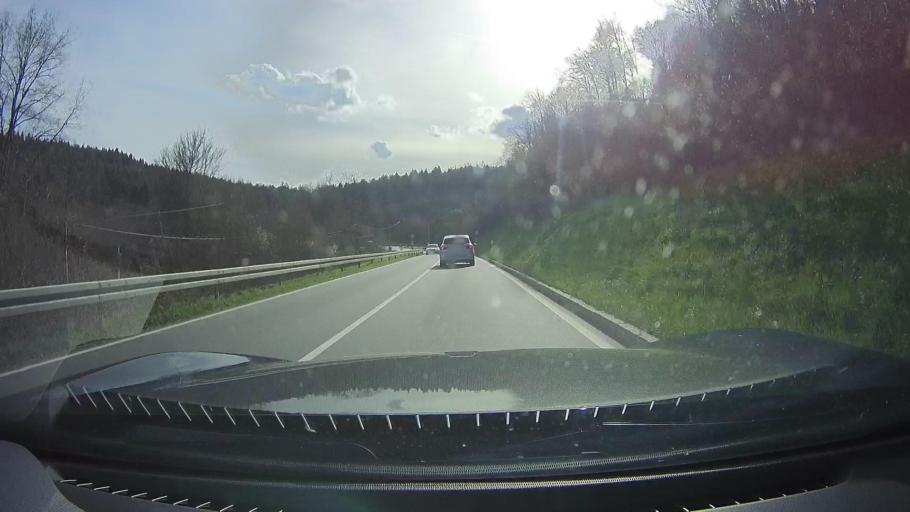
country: DE
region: Baden-Wuerttemberg
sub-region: Karlsruhe Region
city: Walldurn
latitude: 49.6022
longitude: 9.3506
